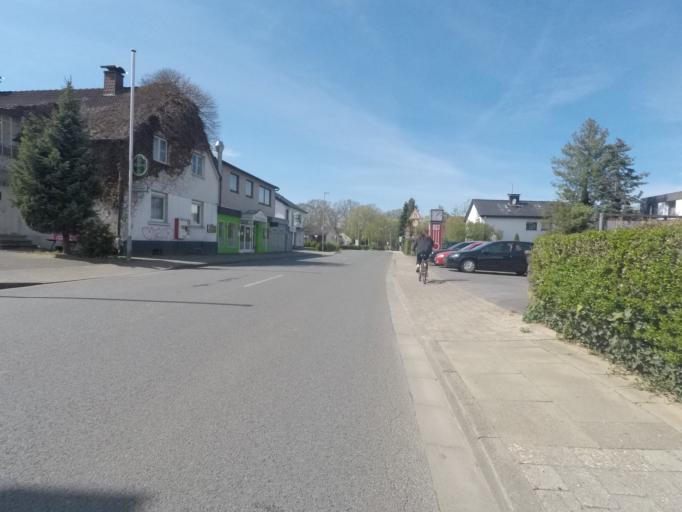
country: DE
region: North Rhine-Westphalia
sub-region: Regierungsbezirk Detmold
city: Leopoldshohe
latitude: 52.0467
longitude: 8.6426
